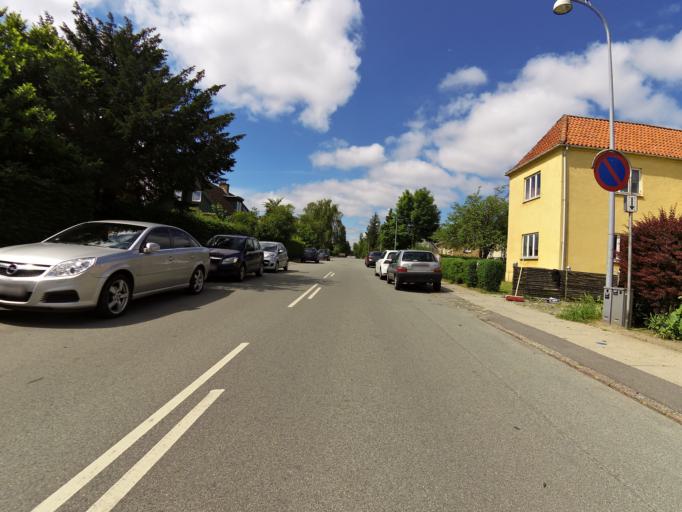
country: DK
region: Capital Region
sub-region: Gladsaxe Municipality
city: Buddinge
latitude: 55.7306
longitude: 12.5101
